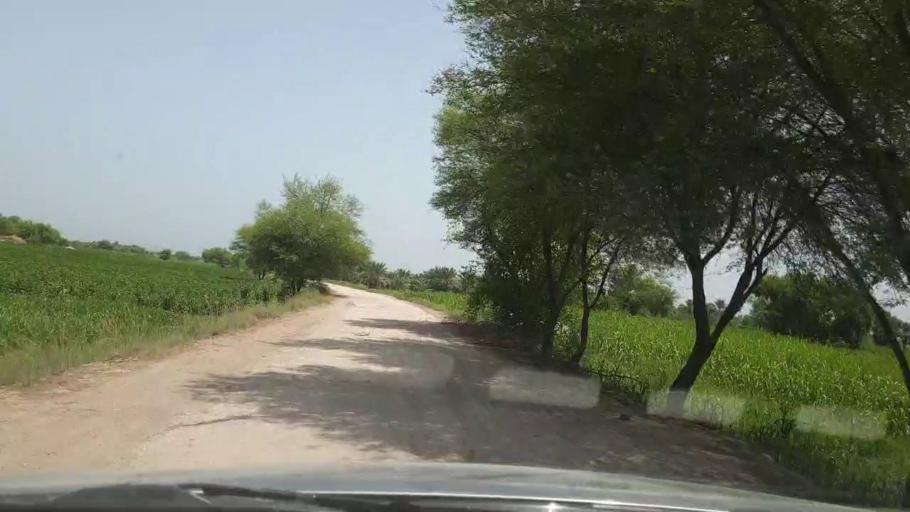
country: PK
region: Sindh
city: Pano Aqil
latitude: 27.8315
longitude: 69.1935
